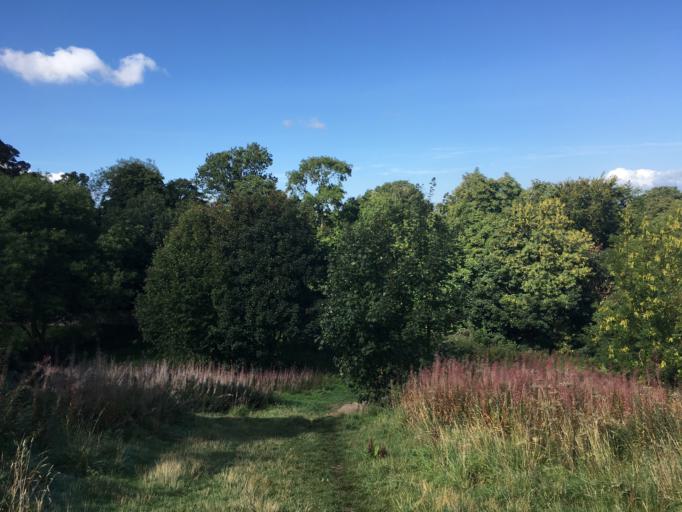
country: GB
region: Scotland
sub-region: Edinburgh
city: Colinton
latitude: 55.9219
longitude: -3.2321
